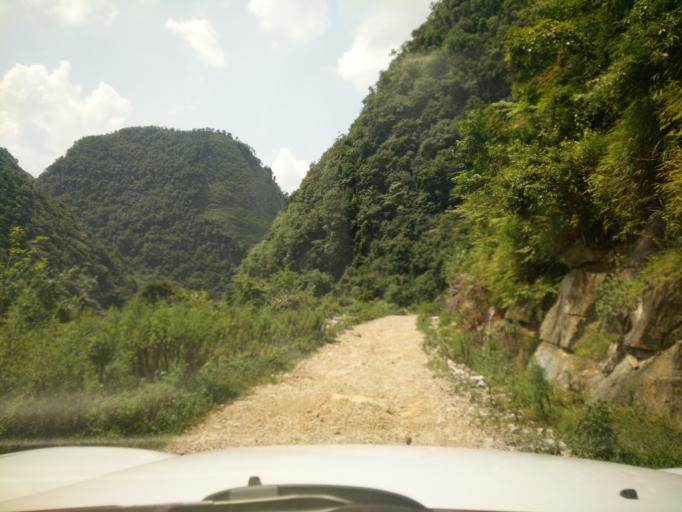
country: CN
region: Guangxi Zhuangzu Zizhiqu
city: Xinzhou
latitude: 25.0123
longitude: 105.7058
